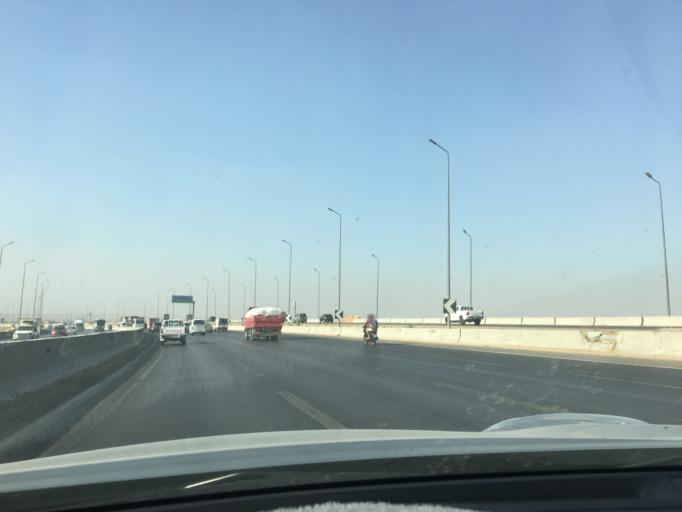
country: EG
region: Muhafazat al Qalyubiyah
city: Al Khankah
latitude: 30.1240
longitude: 31.4646
